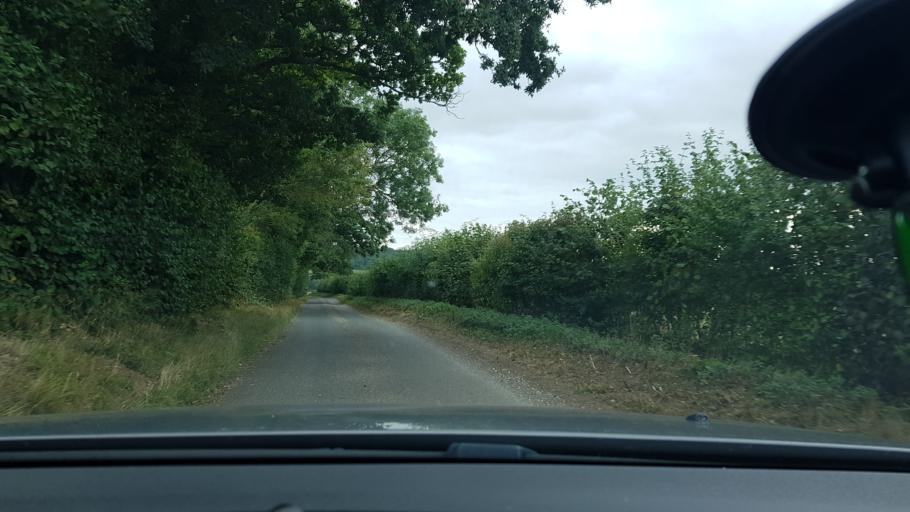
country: GB
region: England
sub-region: Wiltshire
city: Ramsbury
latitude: 51.4490
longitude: -1.5777
